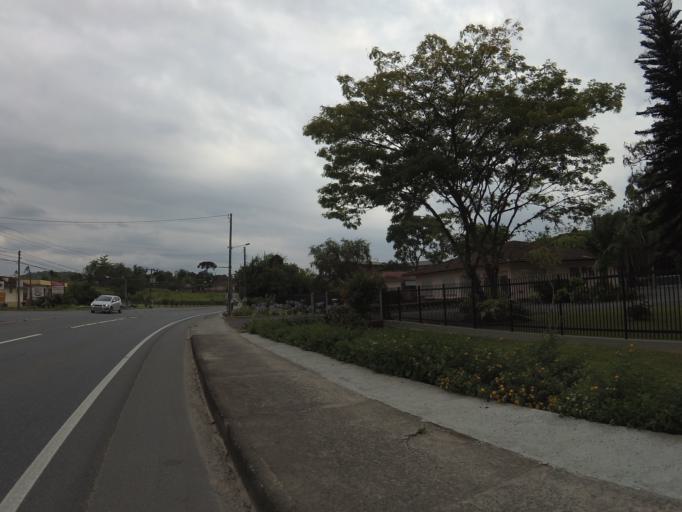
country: BR
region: Santa Catarina
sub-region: Pomerode
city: Pomerode
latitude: -26.8246
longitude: -49.1596
